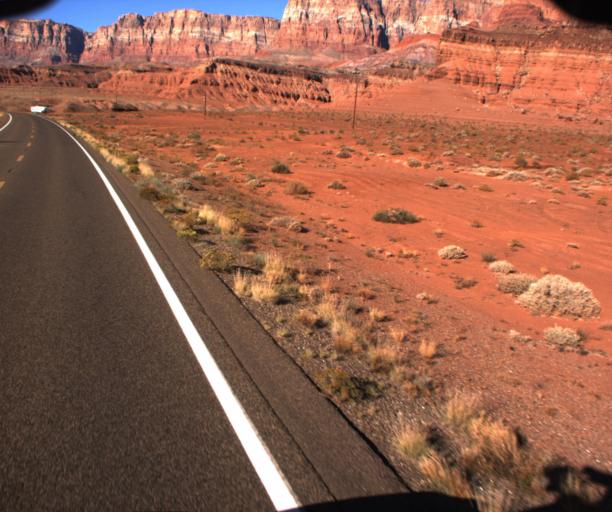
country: US
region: Arizona
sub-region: Coconino County
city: Page
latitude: 36.8131
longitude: -111.6534
